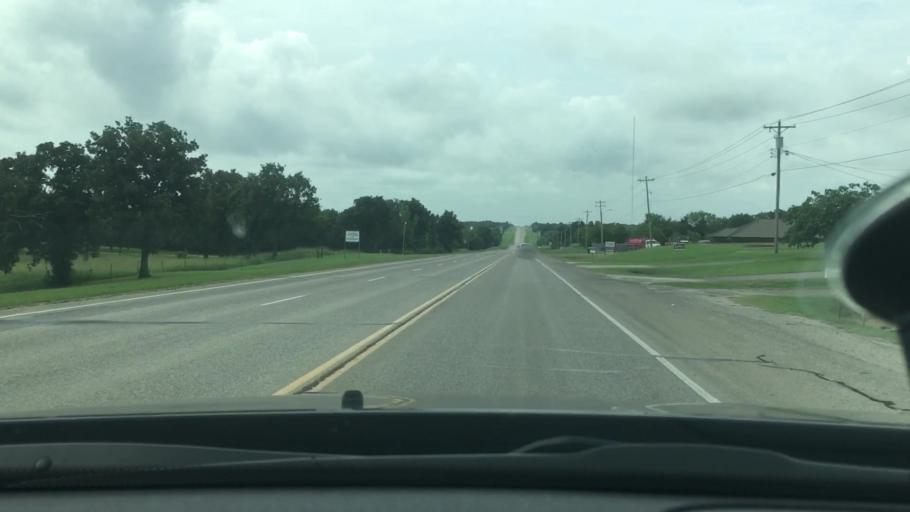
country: US
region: Oklahoma
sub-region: Carter County
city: Healdton
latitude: 34.2151
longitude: -97.4748
